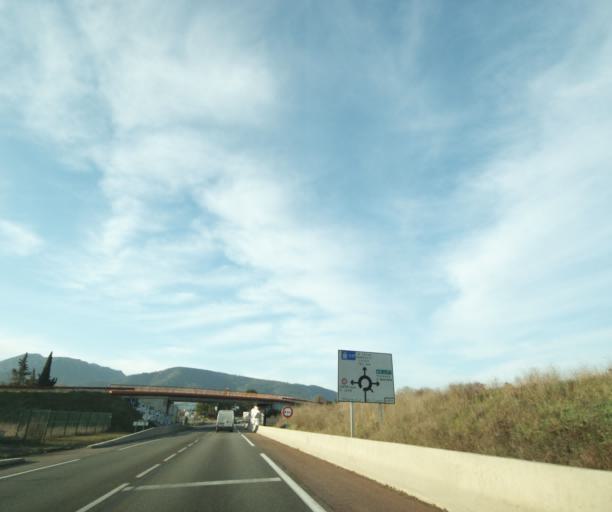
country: FR
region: Provence-Alpes-Cote d'Azur
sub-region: Departement du Var
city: La Celle
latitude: 43.4103
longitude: 6.0447
